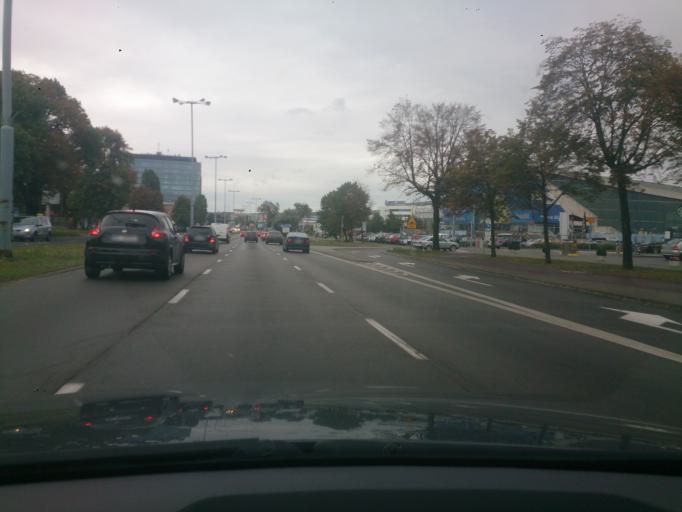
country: PL
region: Pomeranian Voivodeship
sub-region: Sopot
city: Sopot
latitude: 54.4032
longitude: 18.5725
